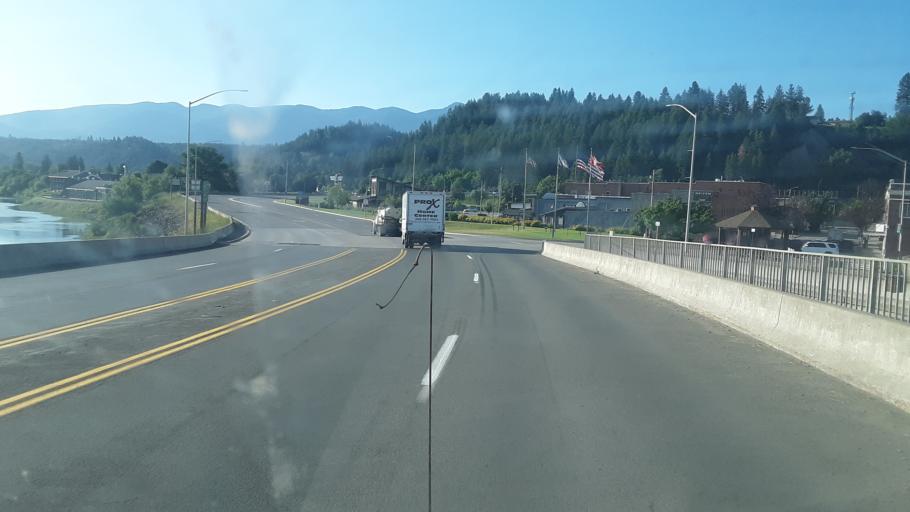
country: US
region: Idaho
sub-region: Boundary County
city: Bonners Ferry
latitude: 48.6986
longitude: -116.3127
